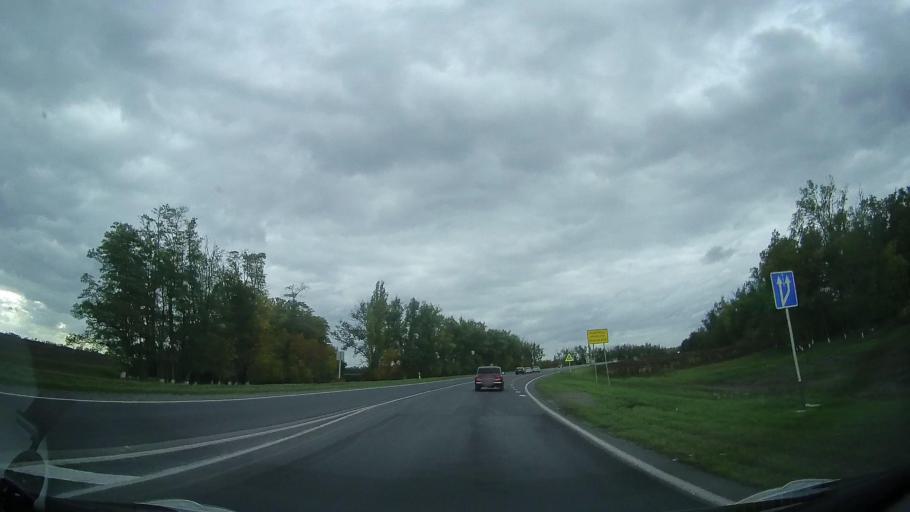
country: RU
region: Rostov
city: Yegorlykskaya
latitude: 46.5375
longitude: 40.7805
